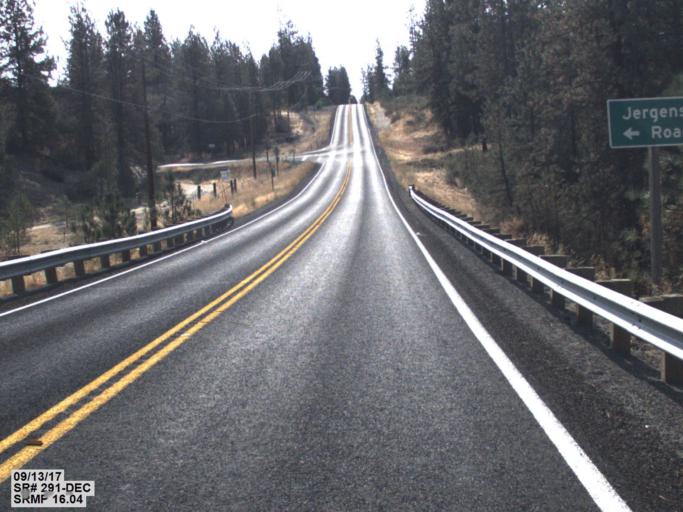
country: US
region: Washington
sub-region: Spokane County
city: Deer Park
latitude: 47.8394
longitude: -117.6085
